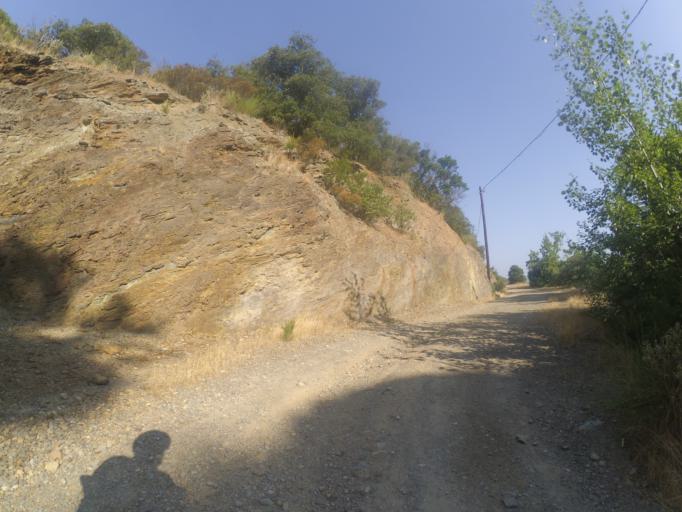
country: FR
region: Languedoc-Roussillon
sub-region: Departement des Pyrenees-Orientales
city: Ille-sur-Tet
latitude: 42.6492
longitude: 2.6497
